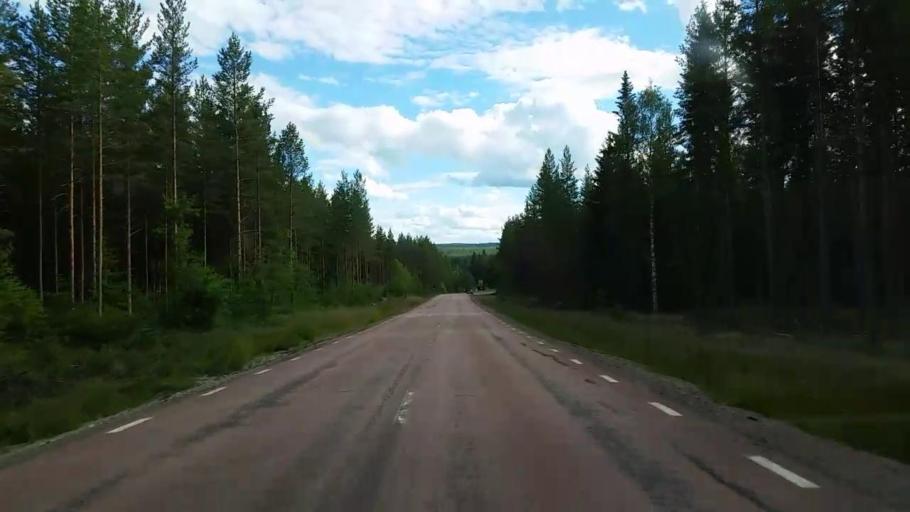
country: SE
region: Gaevleborg
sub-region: Ljusdals Kommun
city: Farila
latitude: 61.9363
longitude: 15.8792
